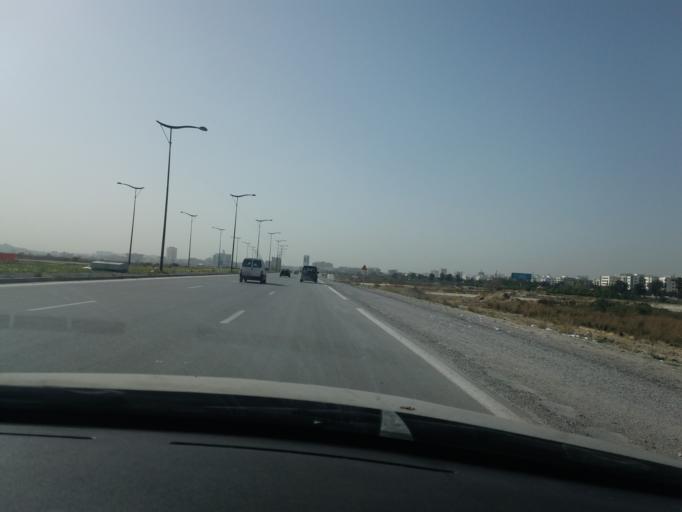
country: TN
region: Tunis
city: Tunis
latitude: 36.8226
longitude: 10.2024
